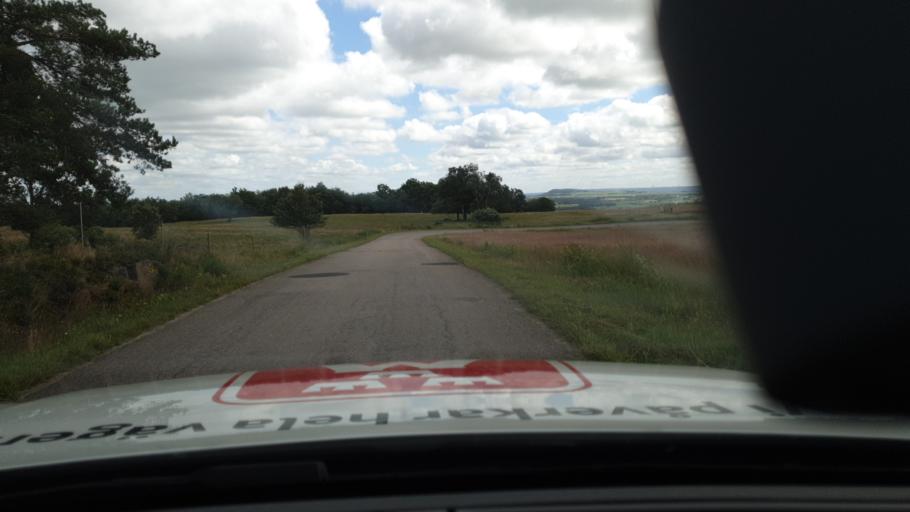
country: SE
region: Vaestra Goetaland
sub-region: Falkopings Kommun
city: Falkoeping
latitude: 58.1378
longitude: 13.6054
